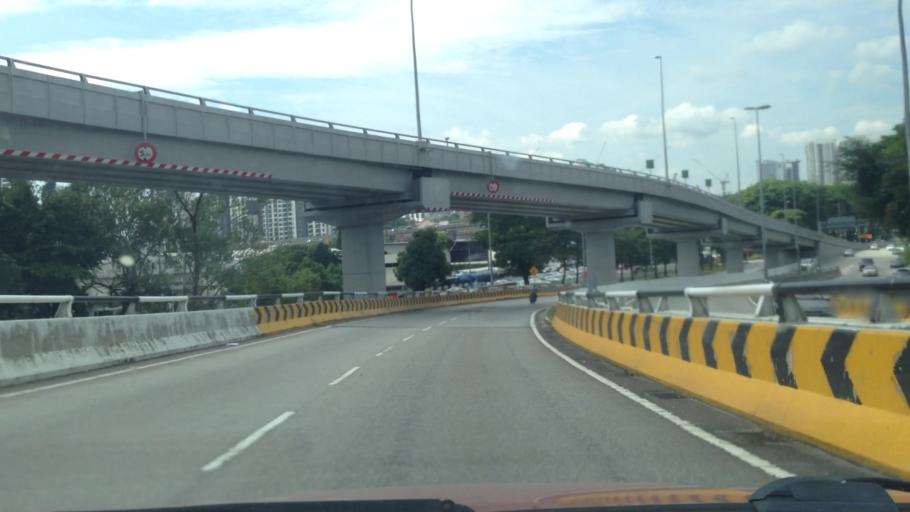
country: MY
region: Kuala Lumpur
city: Kuala Lumpur
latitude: 3.0918
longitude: 101.6909
